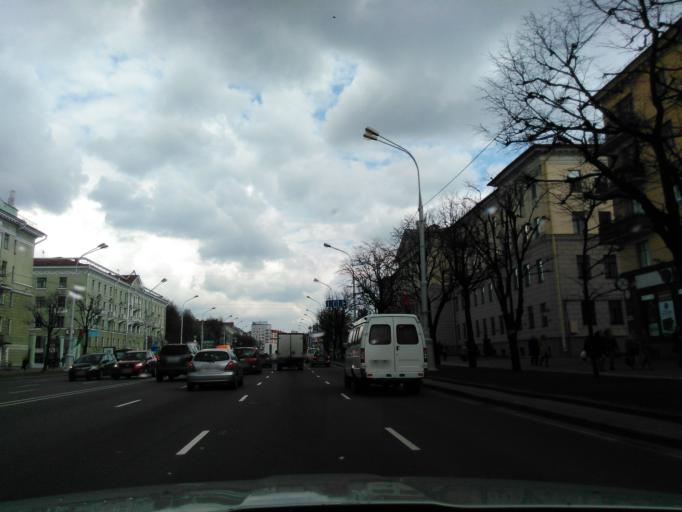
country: BY
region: Minsk
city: Minsk
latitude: 53.9190
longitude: 27.5911
